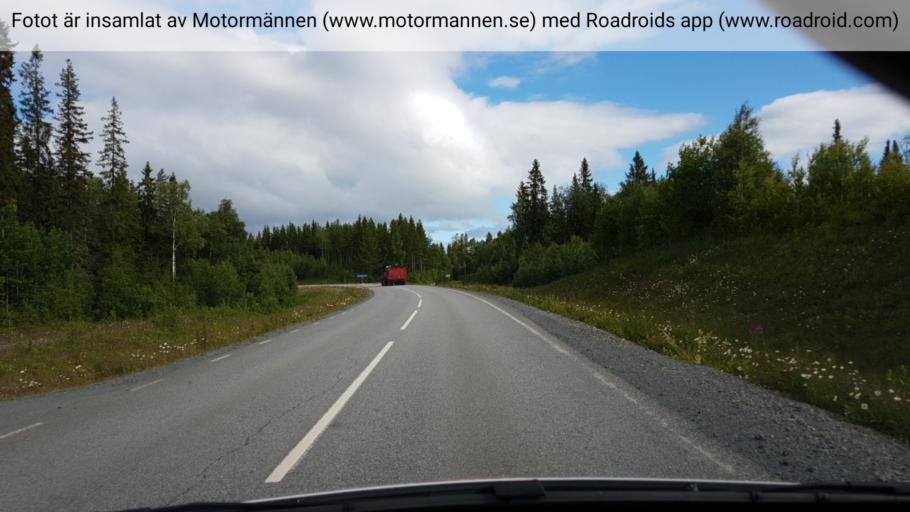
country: SE
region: Jaemtland
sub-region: Krokoms Kommun
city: Krokom
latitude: 63.2864
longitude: 14.4427
